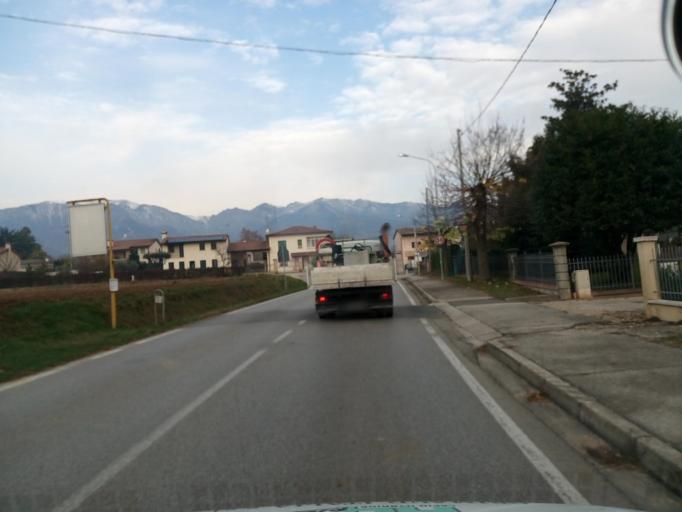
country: IT
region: Veneto
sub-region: Provincia di Treviso
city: Castelcucco
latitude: 45.8104
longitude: 11.8886
